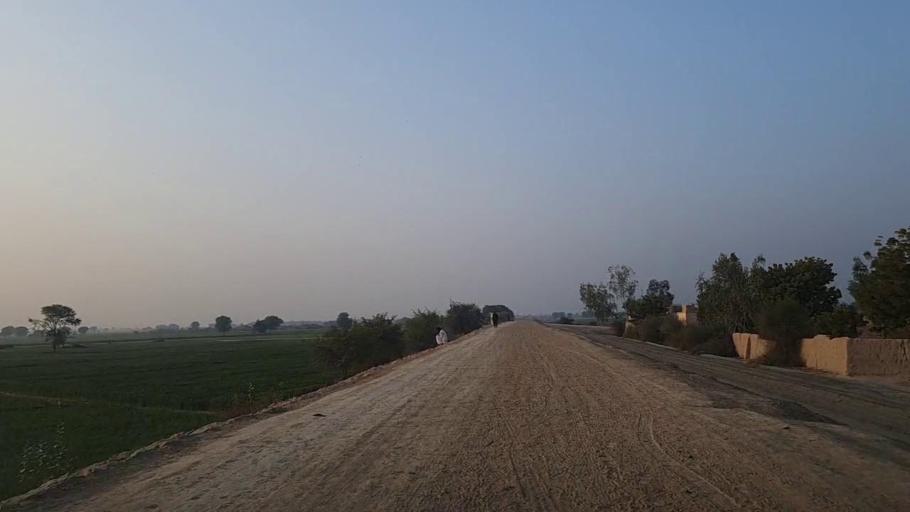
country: PK
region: Sindh
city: Sann
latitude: 26.1935
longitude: 68.0899
